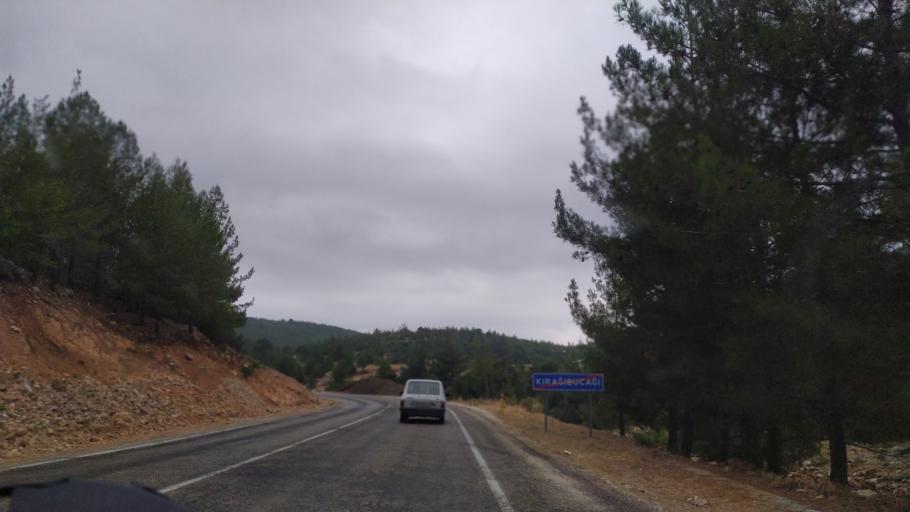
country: TR
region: Mersin
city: Silifke
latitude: 36.5403
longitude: 33.9376
